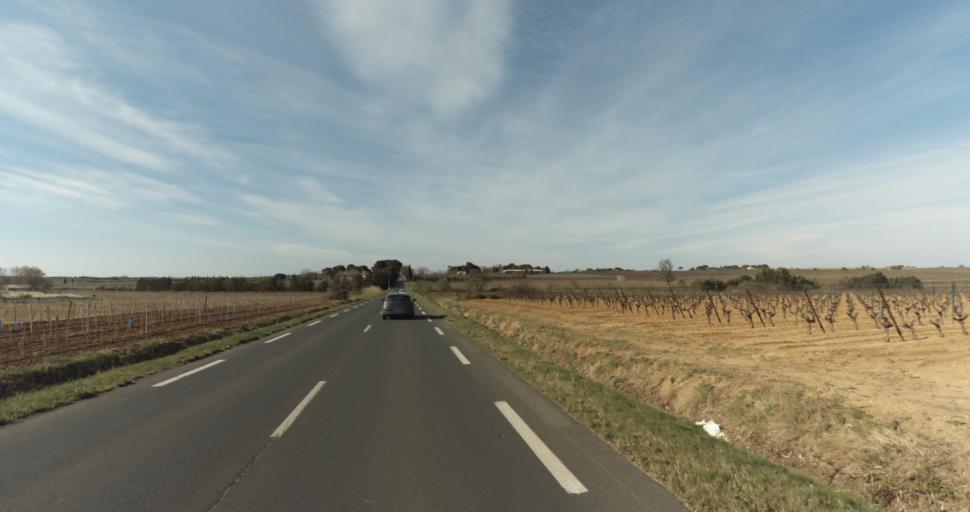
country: FR
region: Languedoc-Roussillon
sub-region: Departement de l'Herault
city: Marseillan
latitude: 43.3440
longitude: 3.5031
